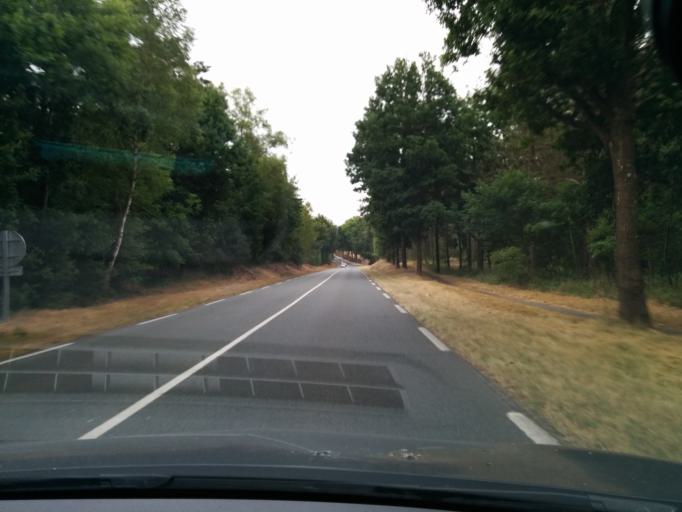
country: FR
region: Ile-de-France
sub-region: Departement des Yvelines
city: Rambouillet
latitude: 48.6719
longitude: 1.7946
